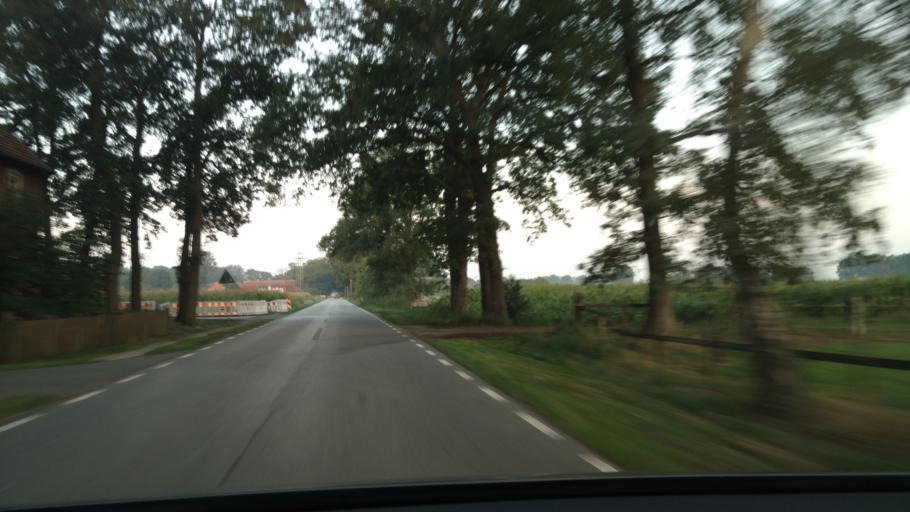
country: DE
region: North Rhine-Westphalia
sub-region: Regierungsbezirk Munster
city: Klein Reken
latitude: 51.8545
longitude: 7.0501
